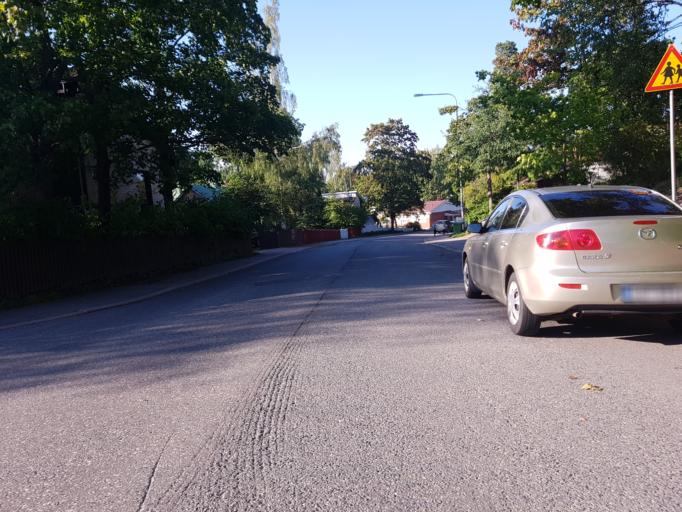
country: FI
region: Uusimaa
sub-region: Helsinki
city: Helsinki
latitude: 60.2272
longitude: 24.9723
